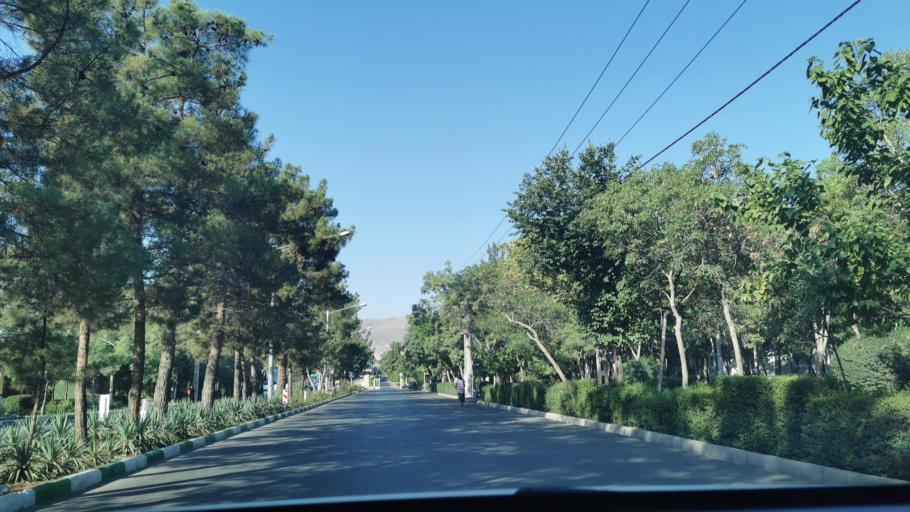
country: IR
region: Razavi Khorasan
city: Mashhad
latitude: 36.3133
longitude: 59.5235
